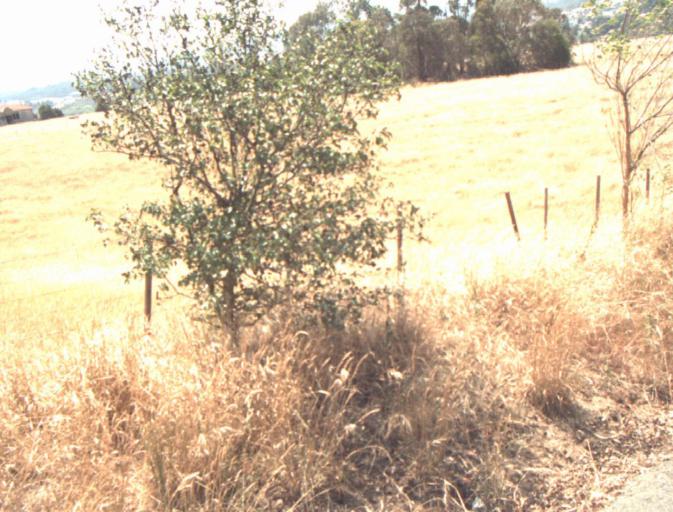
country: AU
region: Tasmania
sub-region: Launceston
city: Newstead
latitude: -41.4703
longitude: 147.1912
